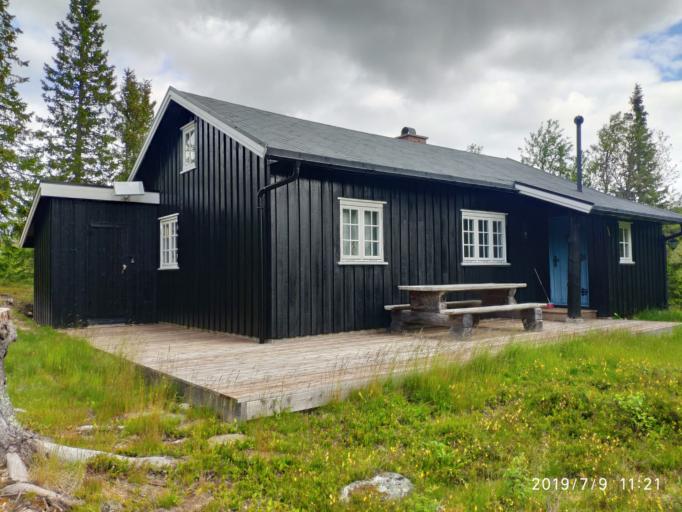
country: NO
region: Buskerud
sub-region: Nore og Uvdal
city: Rodberg
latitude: 60.3336
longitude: 9.1793
